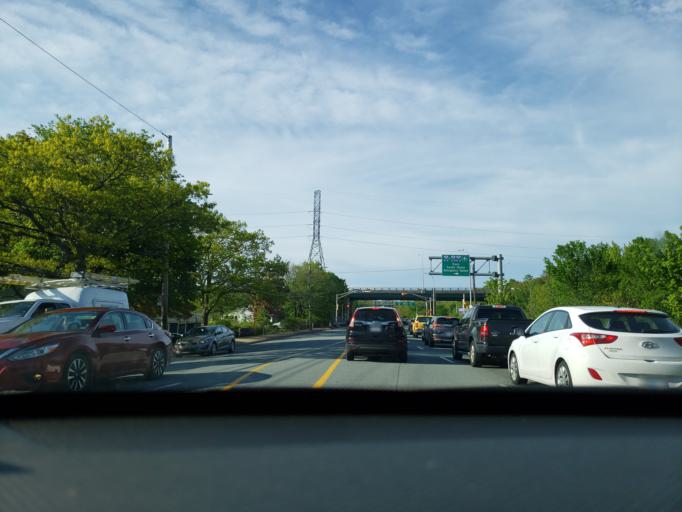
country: CA
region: Nova Scotia
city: Dartmouth
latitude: 44.6530
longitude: -63.6303
